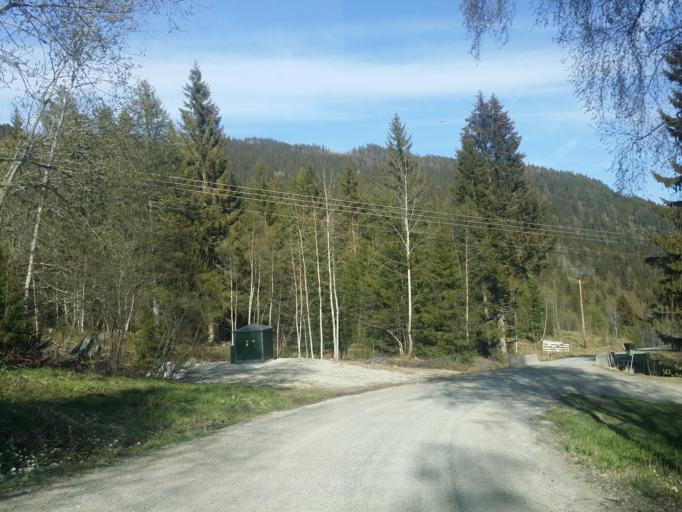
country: NO
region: Telemark
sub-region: Seljord
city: Seljord
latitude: 59.6152
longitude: 8.6879
